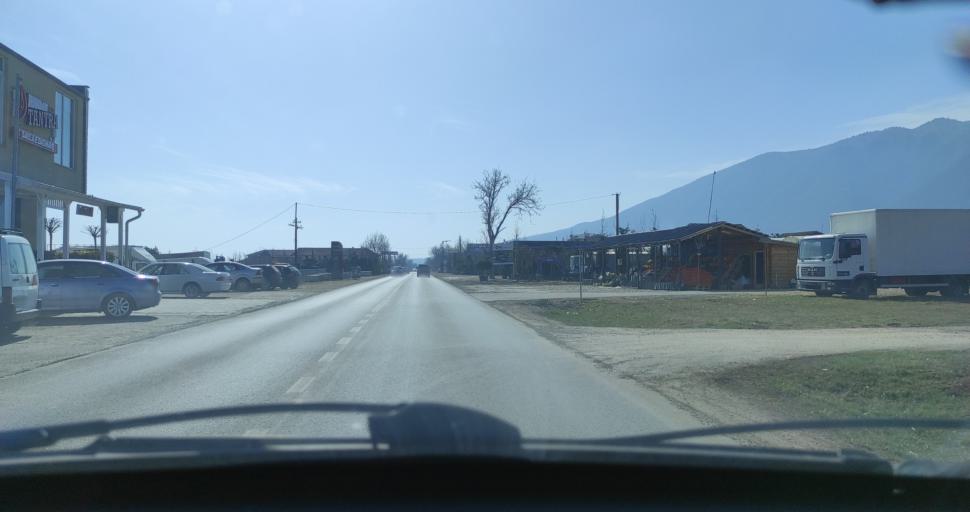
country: XK
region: Pec
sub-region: Komuna e Pejes
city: Peje
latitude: 42.6242
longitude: 20.3050
